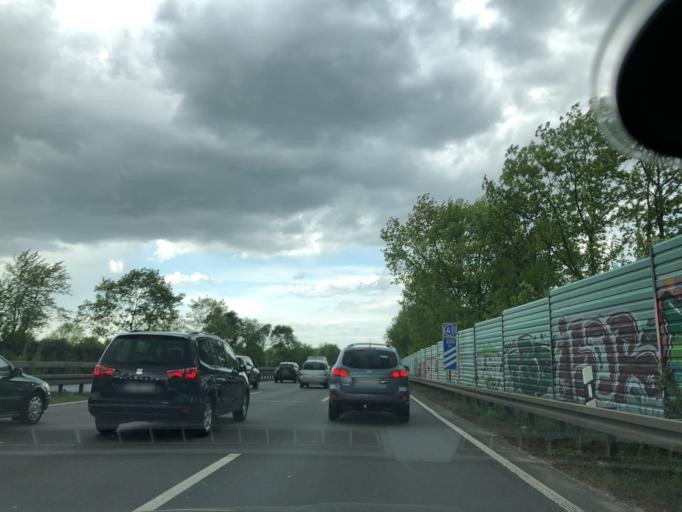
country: DE
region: North Rhine-Westphalia
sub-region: Regierungsbezirk Koln
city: Bonn
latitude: 50.7438
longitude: 7.1432
